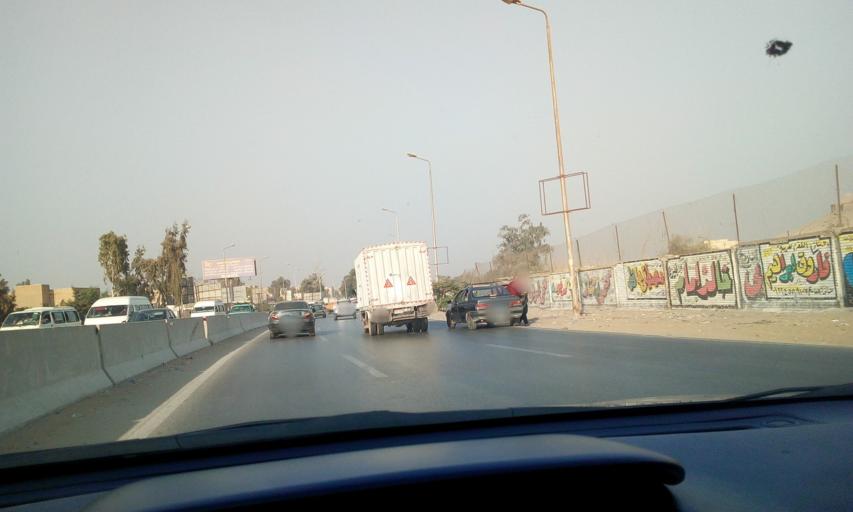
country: EG
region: Al Jizah
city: Al Jizah
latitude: 29.9776
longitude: 31.1124
